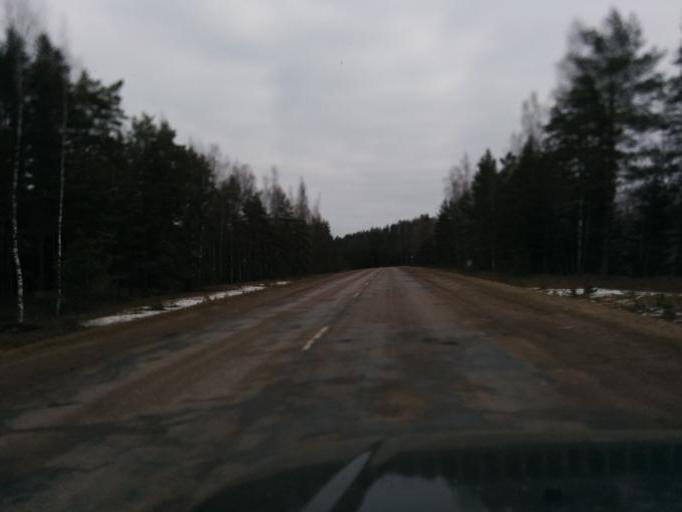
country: LV
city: Tireli
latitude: 56.8626
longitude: 23.5404
